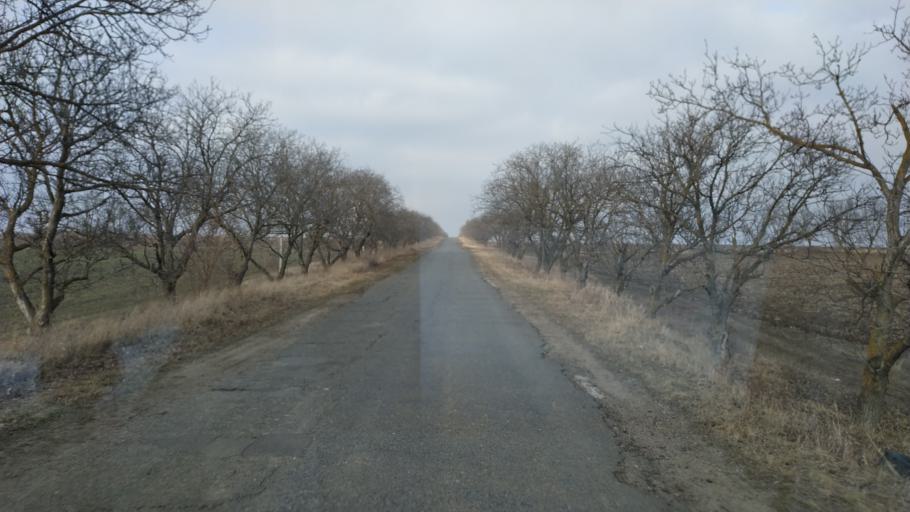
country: MD
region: Hincesti
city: Dancu
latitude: 46.8735
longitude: 28.2955
